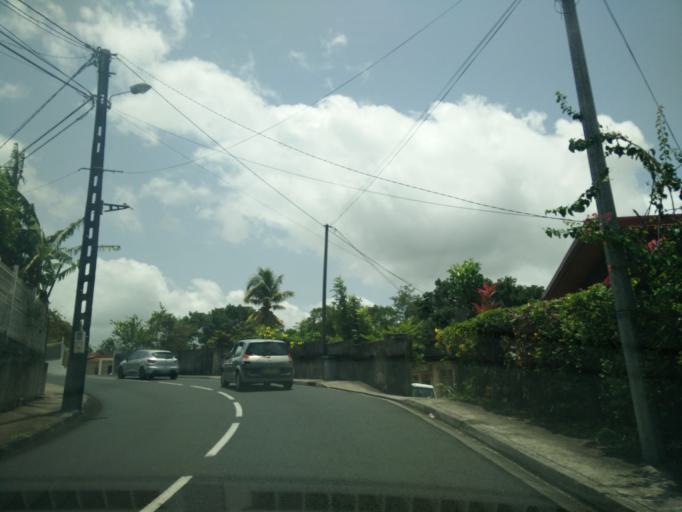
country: MQ
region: Martinique
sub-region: Martinique
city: Fort-de-France
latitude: 14.6306
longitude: -61.0724
